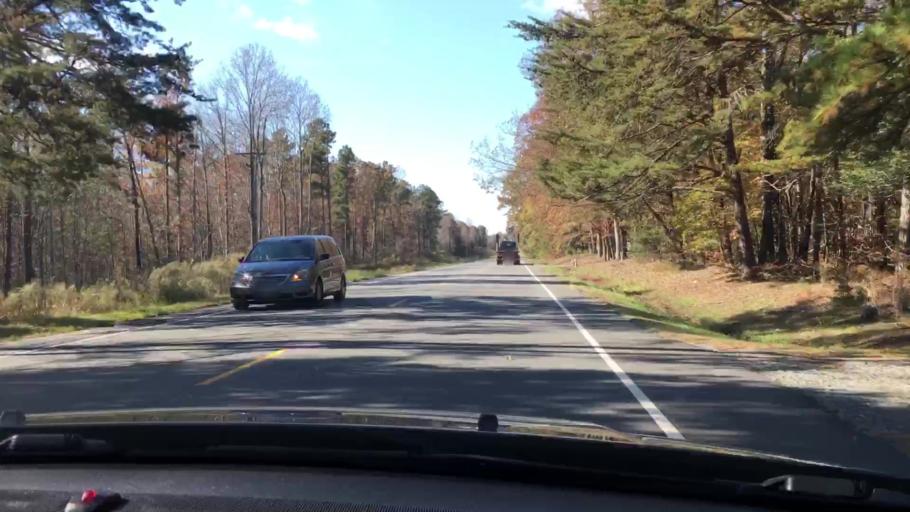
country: US
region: Virginia
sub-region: Hanover County
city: Hanover
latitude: 37.7966
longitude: -77.2505
